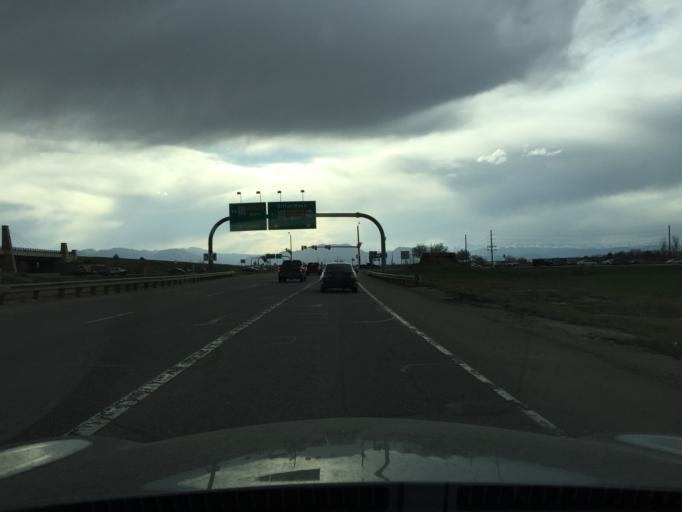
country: US
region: Colorado
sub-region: Boulder County
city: Lafayette
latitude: 39.9597
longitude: -105.0883
